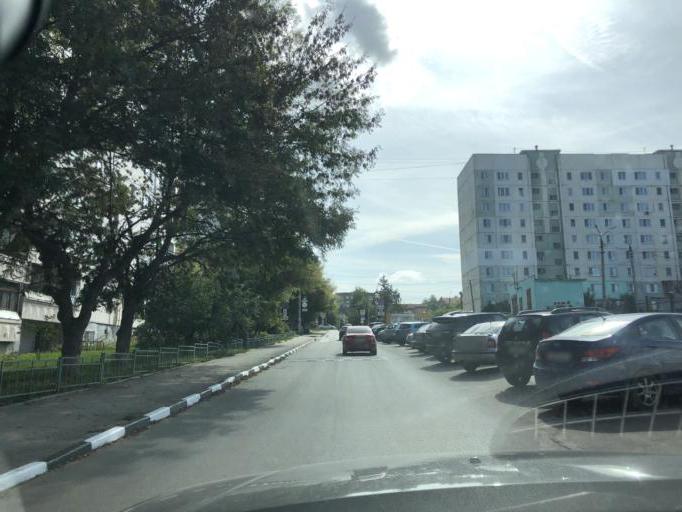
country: RU
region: Tula
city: Tula
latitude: 54.2044
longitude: 37.6464
